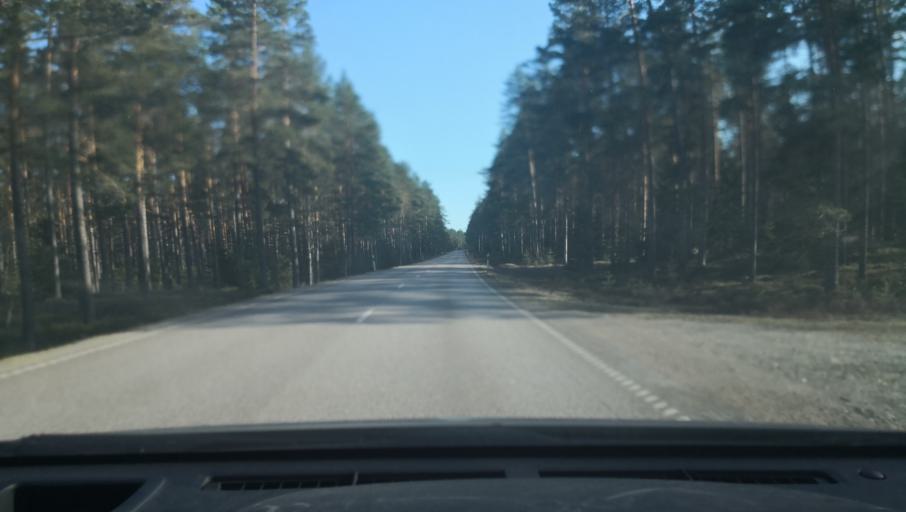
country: SE
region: Uppsala
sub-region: Heby Kommun
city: Tarnsjo
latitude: 60.1147
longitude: 16.8855
